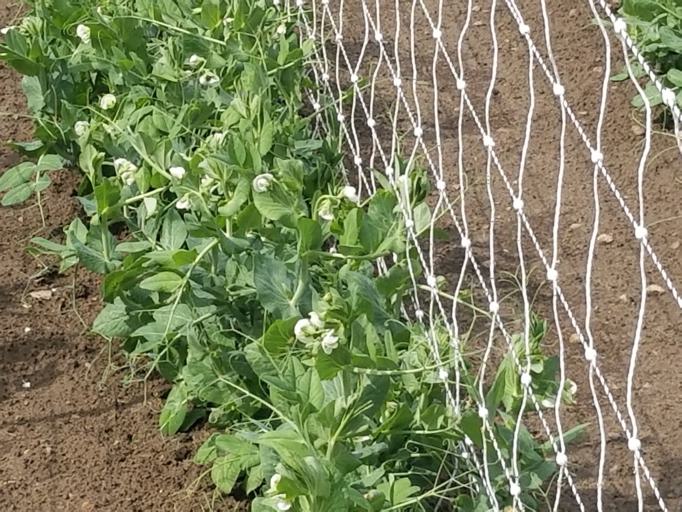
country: US
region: Indiana
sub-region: Elkhart County
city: Nappanee
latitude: 41.4772
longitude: -86.0517
